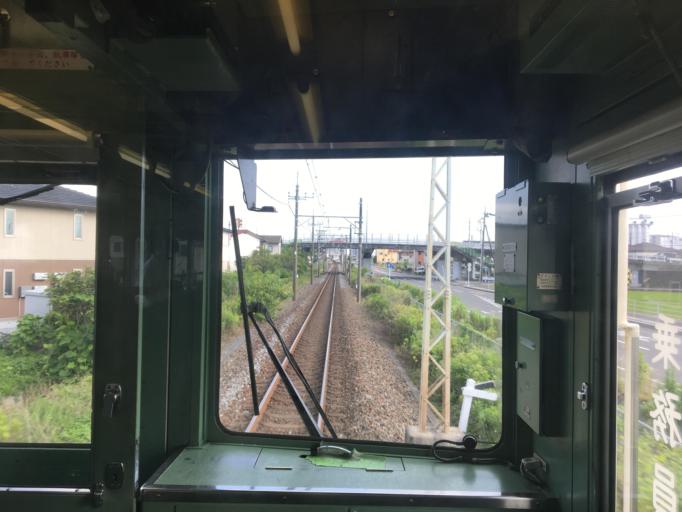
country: JP
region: Tochigi
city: Ashikaga
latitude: 36.3184
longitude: 139.4544
